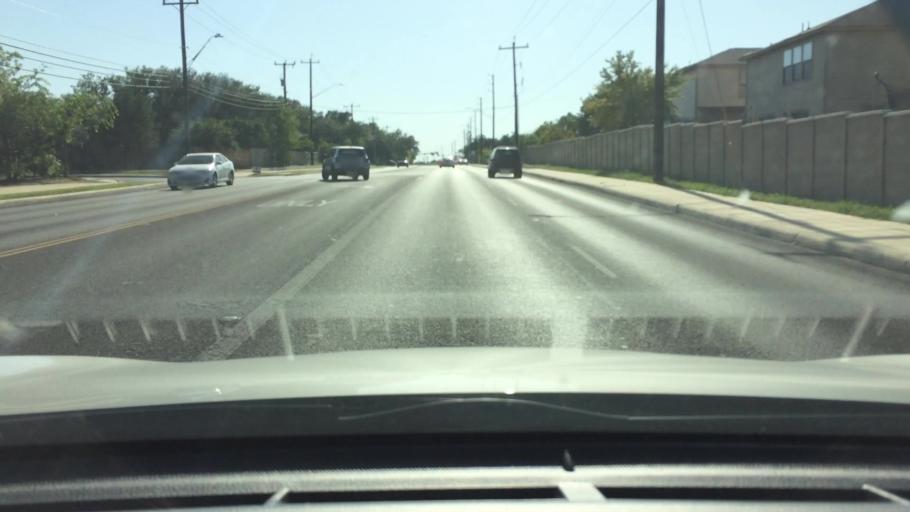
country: US
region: Texas
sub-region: Bexar County
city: Helotes
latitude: 29.5710
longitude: -98.6394
